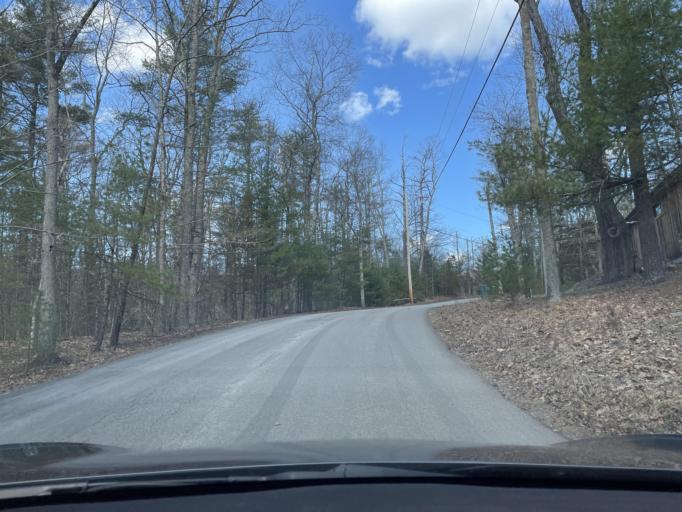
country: US
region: New York
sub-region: Ulster County
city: West Hurley
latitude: 41.9578
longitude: -74.1130
